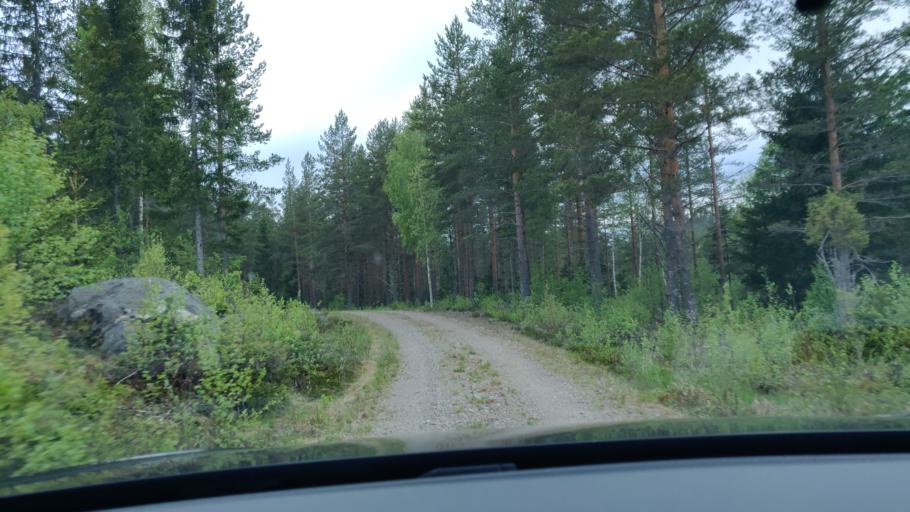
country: SE
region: Gaevleborg
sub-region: Gavle Kommun
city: Valbo
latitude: 60.8023
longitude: 16.9110
